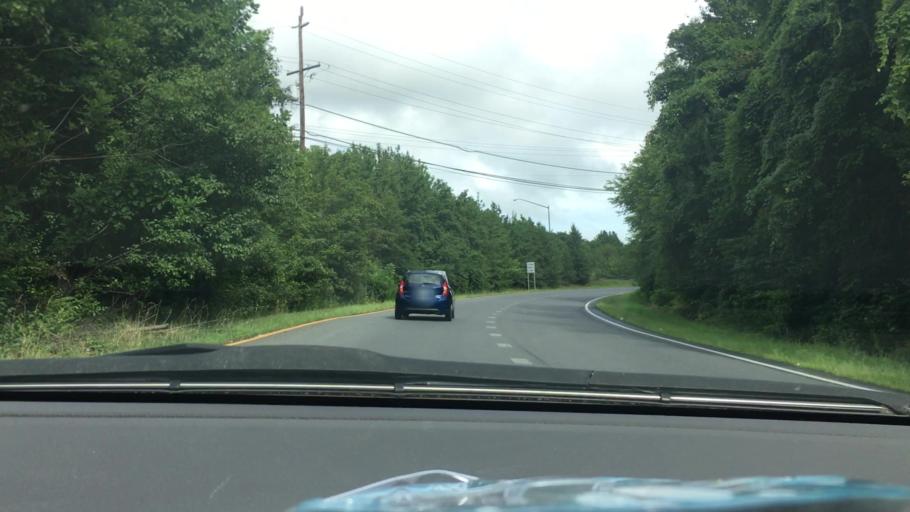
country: US
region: Maryland
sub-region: Montgomery County
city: Germantown
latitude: 39.1740
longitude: -77.2474
